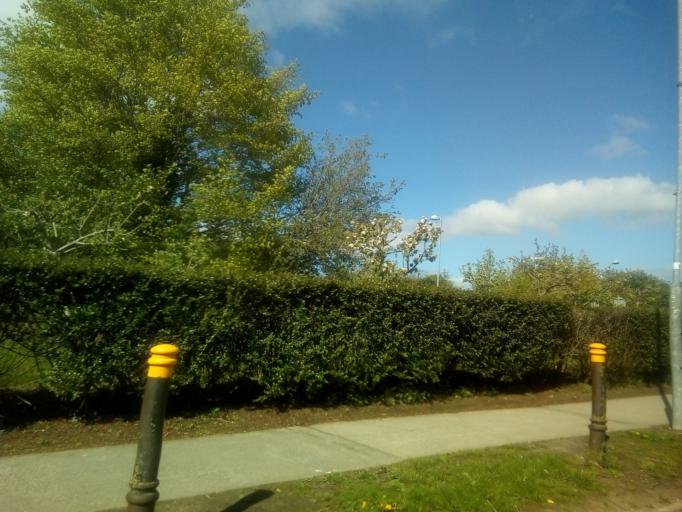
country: IE
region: Leinster
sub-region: Kildare
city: Maynooth
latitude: 53.3835
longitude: -6.6034
